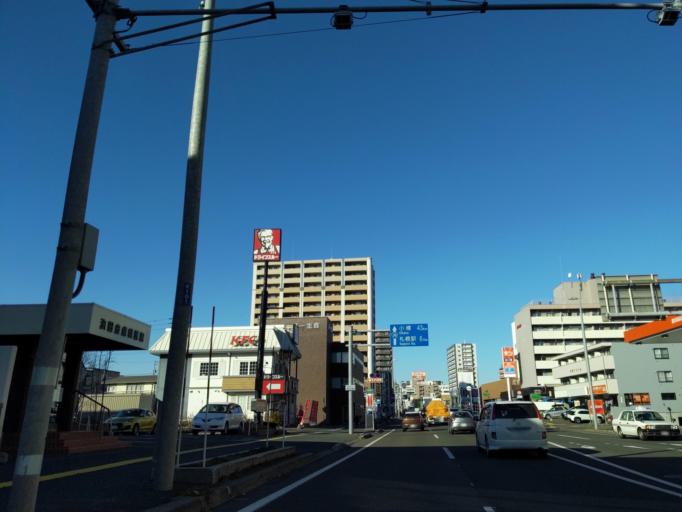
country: JP
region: Hokkaido
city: Sapporo
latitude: 43.0256
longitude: 141.3990
